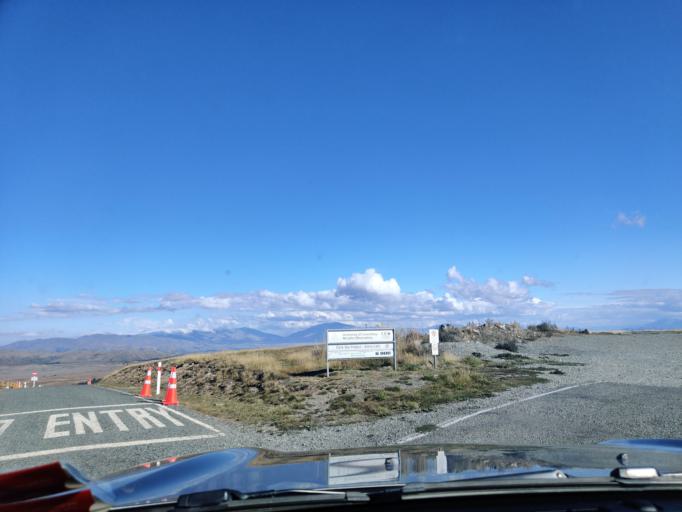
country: NZ
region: Canterbury
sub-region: Timaru District
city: Pleasant Point
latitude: -43.9858
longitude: 170.4640
